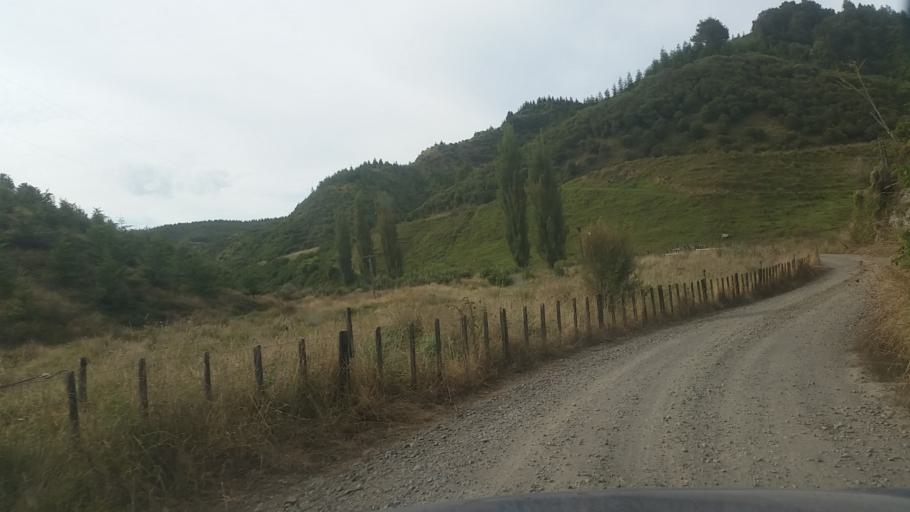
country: NZ
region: Taranaki
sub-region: New Plymouth District
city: Waitara
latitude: -39.1314
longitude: 174.7023
